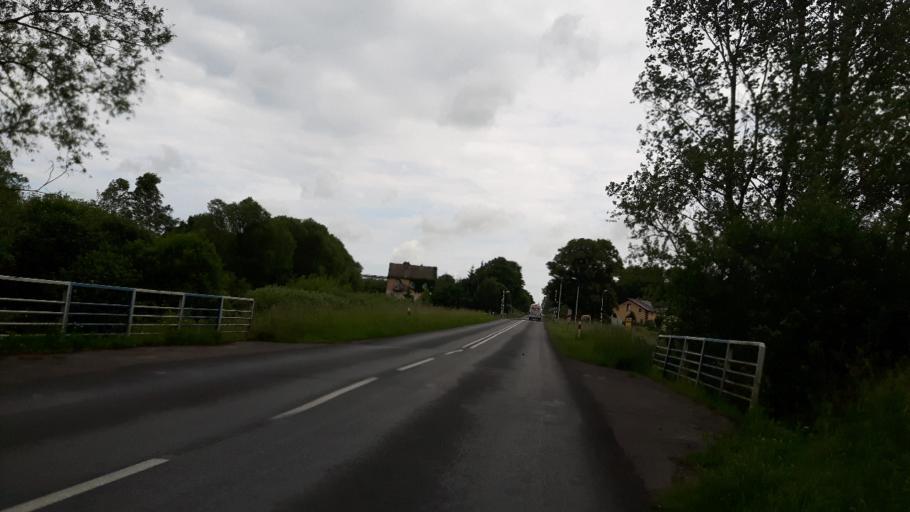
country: PL
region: West Pomeranian Voivodeship
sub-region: Powiat gryficki
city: Gryfice
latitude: 53.9680
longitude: 15.2317
